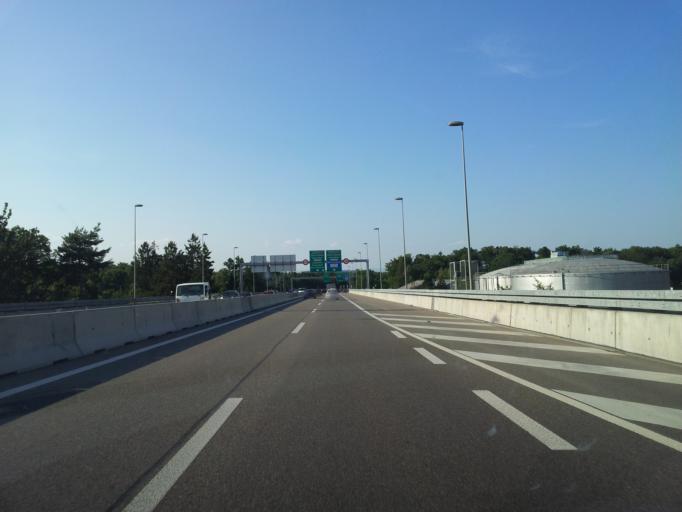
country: CH
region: Bern
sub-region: Bern-Mittelland District
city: Koniz
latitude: 46.9468
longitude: 7.4068
